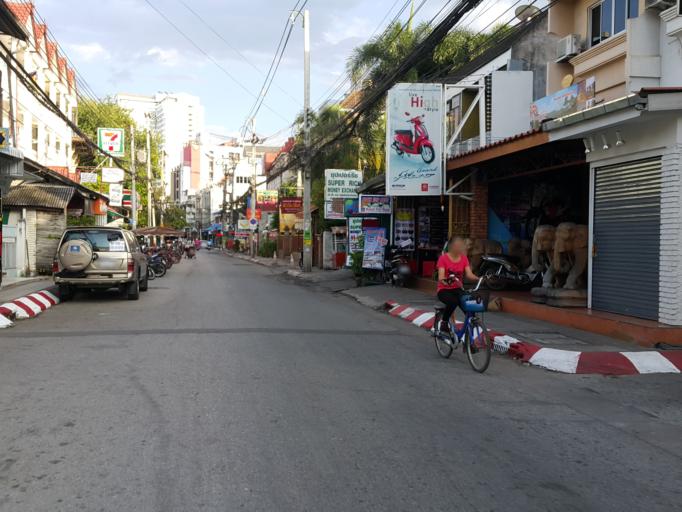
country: TH
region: Chiang Mai
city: Chiang Mai
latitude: 18.7847
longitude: 98.9950
